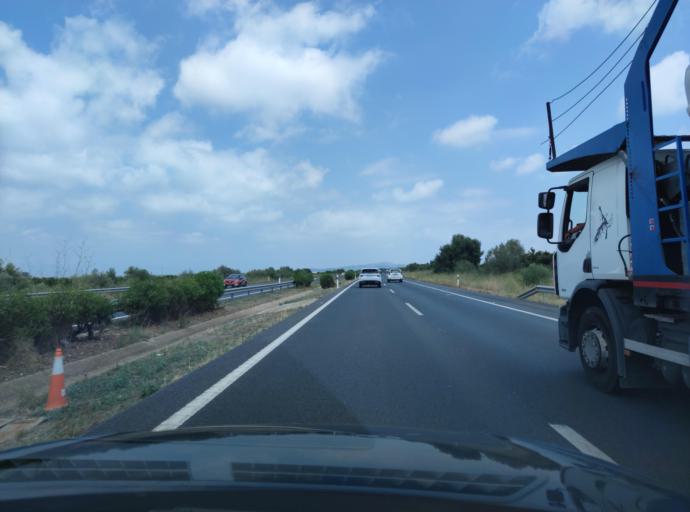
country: ES
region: Catalonia
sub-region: Provincia de Tarragona
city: Alcanar
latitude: 40.5164
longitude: 0.4157
